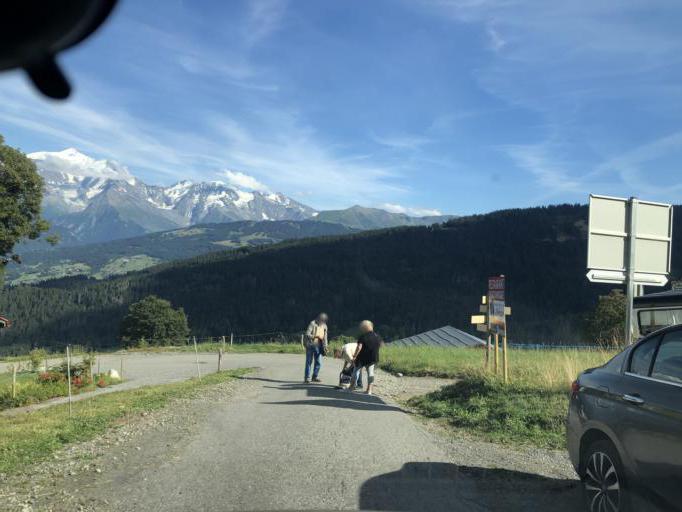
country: FR
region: Rhone-Alpes
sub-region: Departement de la Haute-Savoie
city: Cordon
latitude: 45.9116
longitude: 6.5885
